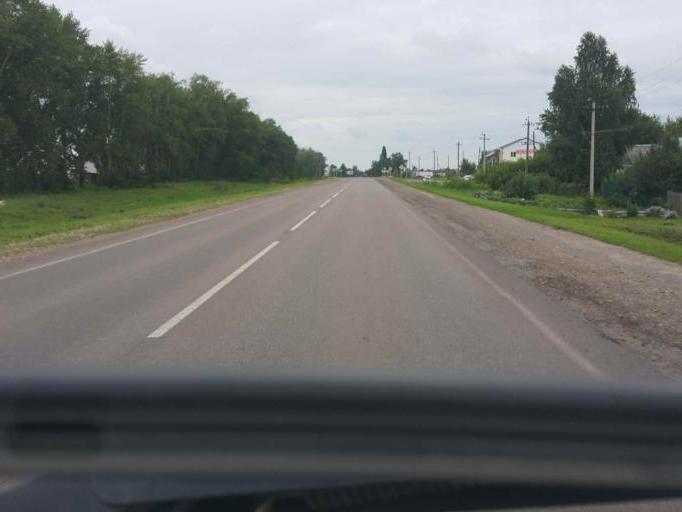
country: RU
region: Tambov
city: Zavoronezhskoye
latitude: 52.8905
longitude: 40.5708
